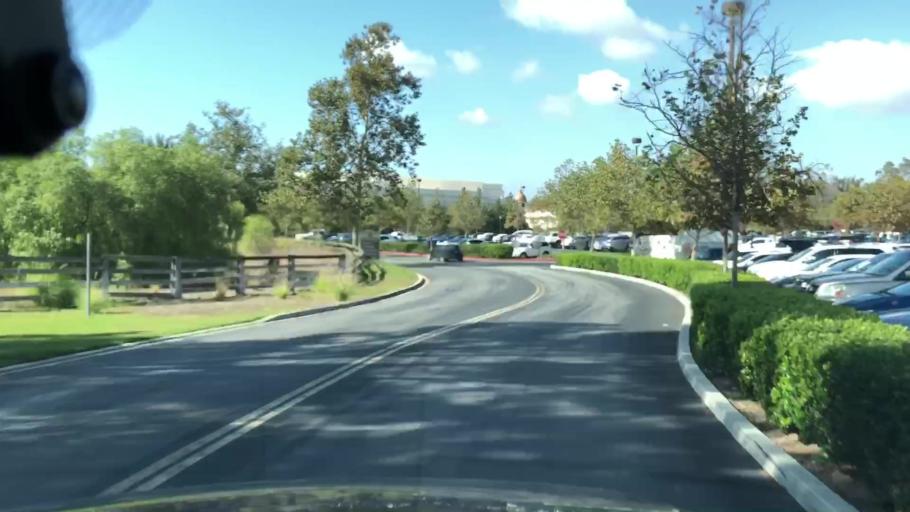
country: US
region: California
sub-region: Ventura County
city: Thousand Oaks
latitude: 34.1803
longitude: -118.8840
